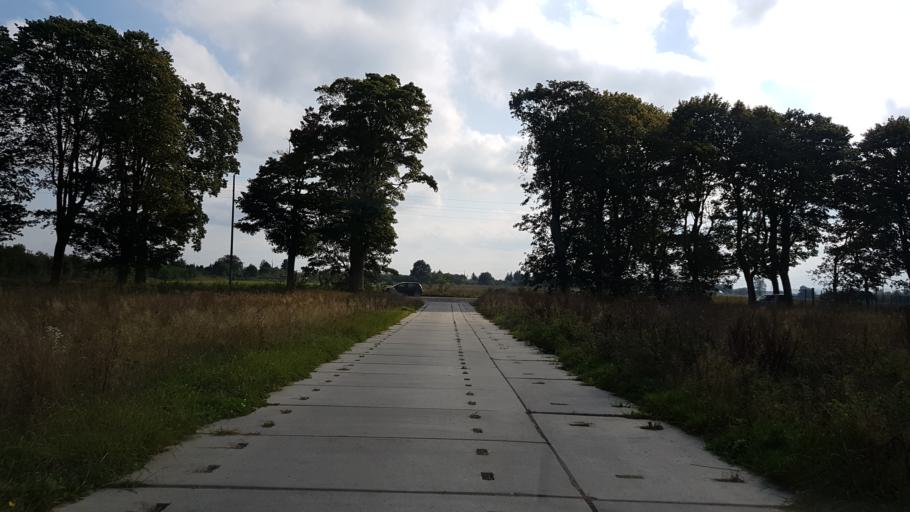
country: PL
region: West Pomeranian Voivodeship
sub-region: Koszalin
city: Koszalin
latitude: 54.1745
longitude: 16.1598
